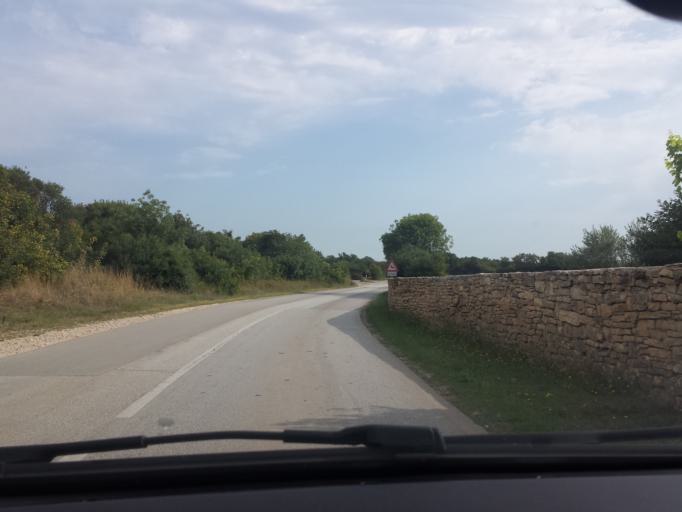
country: HR
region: Istarska
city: Galizana
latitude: 44.9087
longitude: 13.8557
